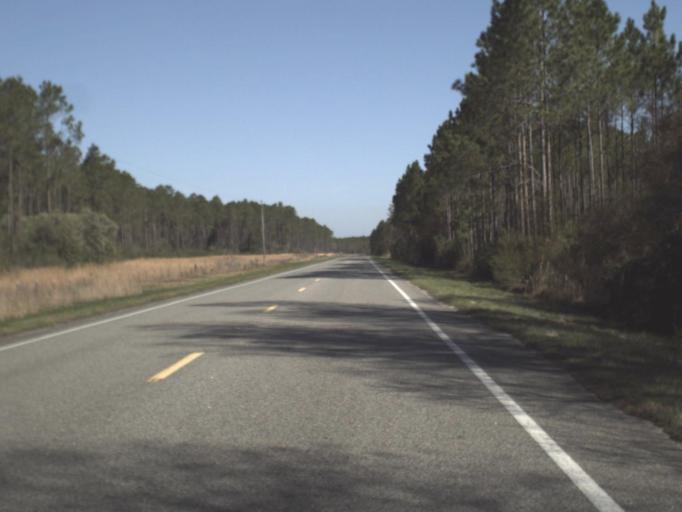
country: US
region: Florida
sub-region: Leon County
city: Woodville
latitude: 30.2757
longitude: -84.0423
